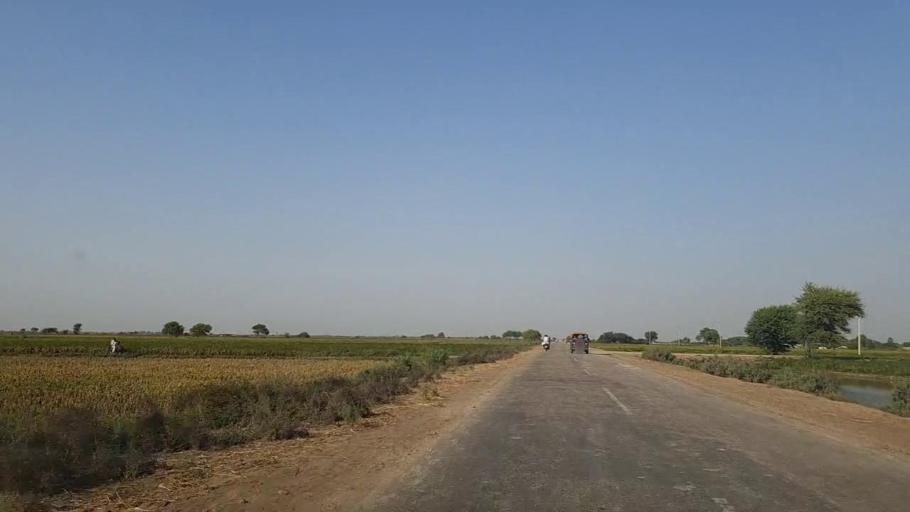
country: PK
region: Sindh
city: Mirpur Batoro
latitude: 24.5898
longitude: 68.3980
